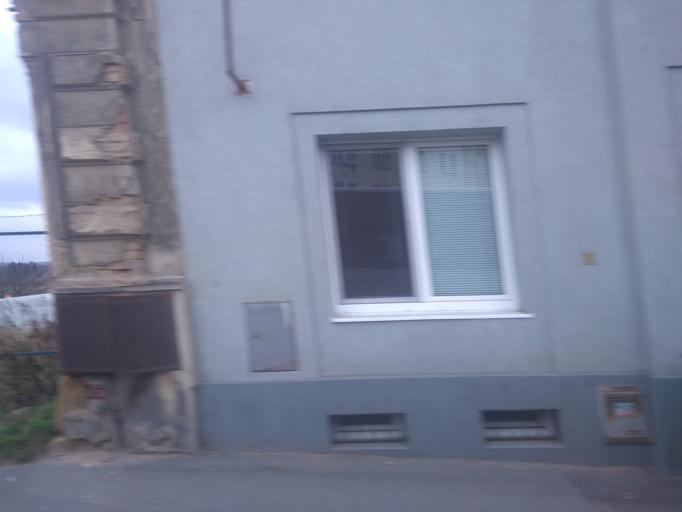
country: CZ
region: Plzensky
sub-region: Okres Plzen-Mesto
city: Pilsen
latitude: 49.7468
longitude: 13.3594
